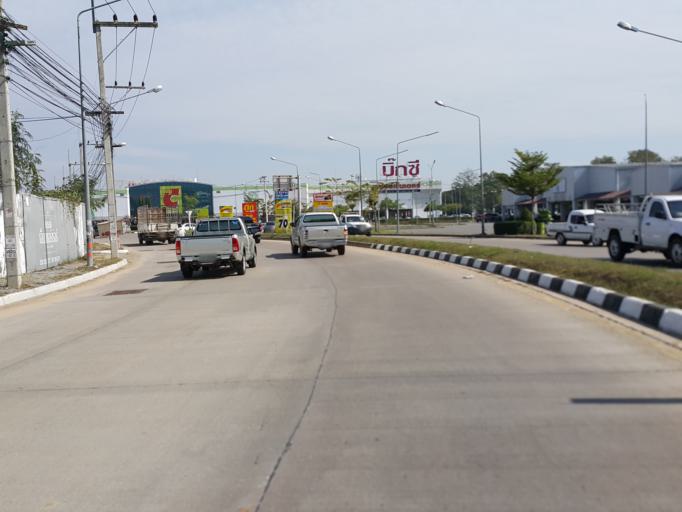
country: TH
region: Chiang Mai
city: Chiang Mai
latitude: 18.7689
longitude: 99.0306
